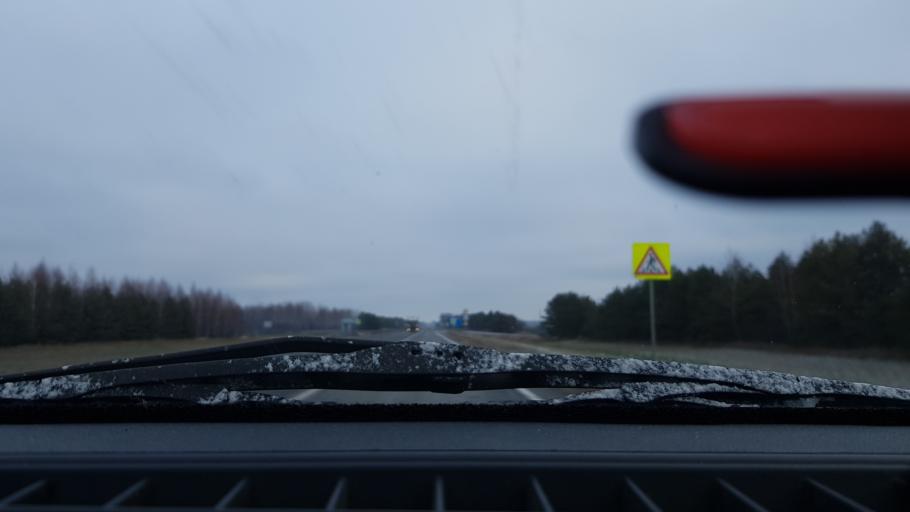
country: RU
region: Tatarstan
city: Kuybyshevskiy Zaton
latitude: 54.9628
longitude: 49.4954
